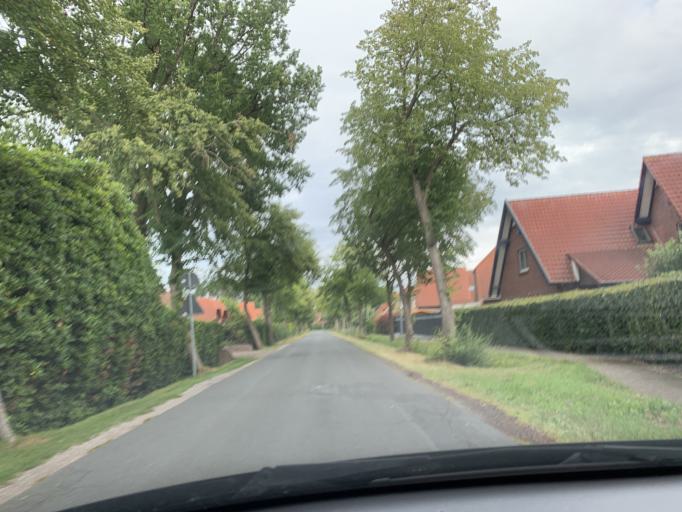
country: DE
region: Lower Saxony
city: Westerstede
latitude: 53.2553
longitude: 7.9000
